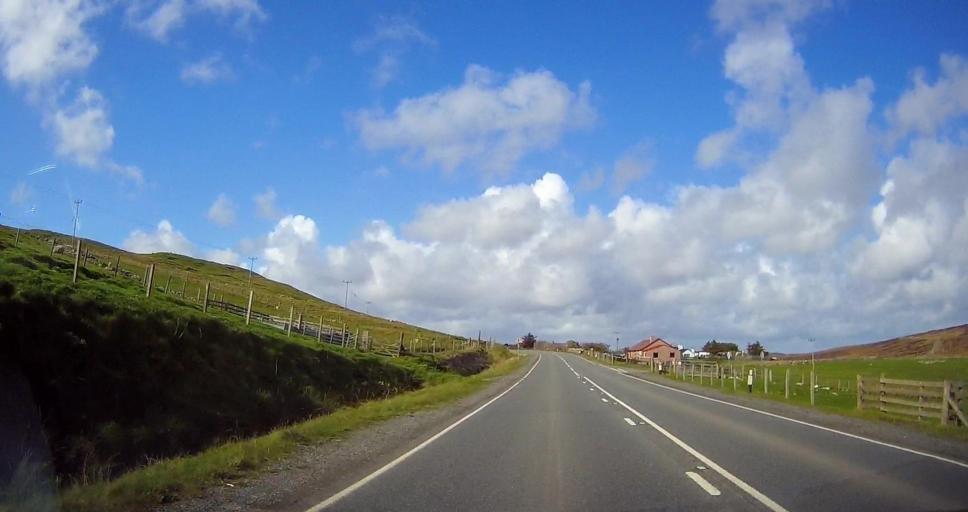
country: GB
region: Scotland
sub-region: Shetland Islands
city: Lerwick
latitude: 60.2385
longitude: -1.2297
